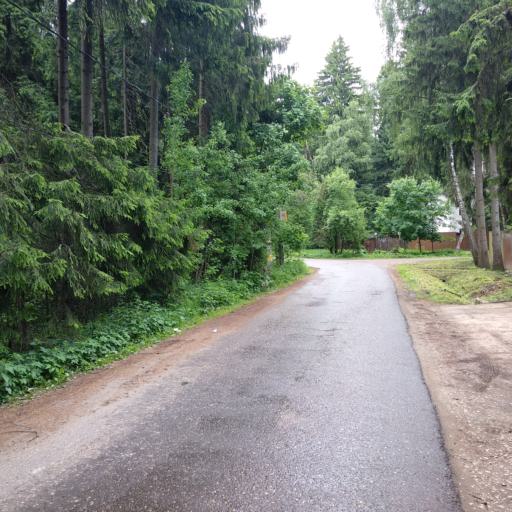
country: RU
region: Moskovskaya
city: Nekrasovskiy
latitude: 56.1204
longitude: 37.5171
